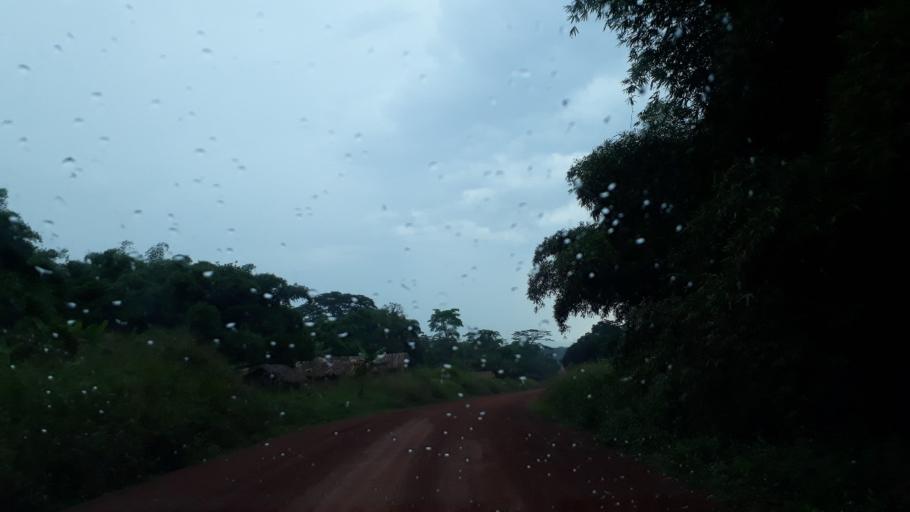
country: CD
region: Eastern Province
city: Kisangani
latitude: 0.4635
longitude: 25.4597
